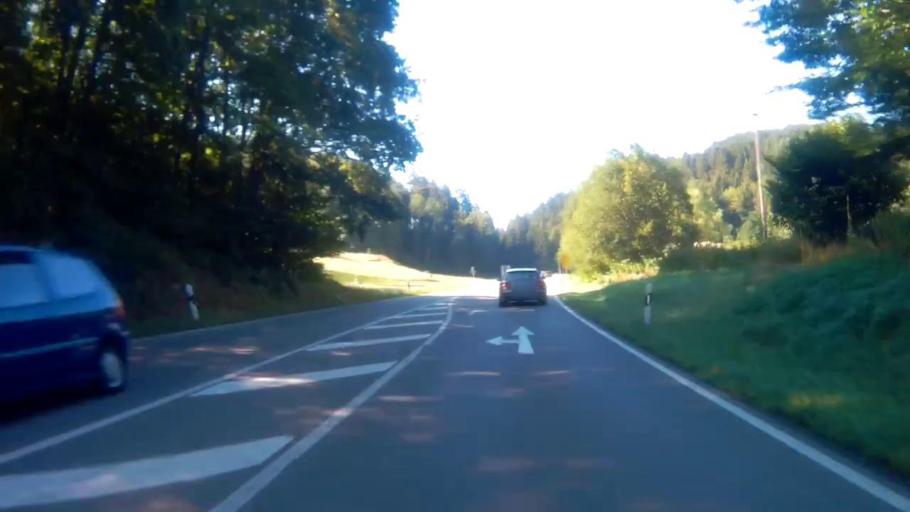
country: DE
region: Baden-Wuerttemberg
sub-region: Freiburg Region
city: Wembach
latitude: 47.7698
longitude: 7.8871
